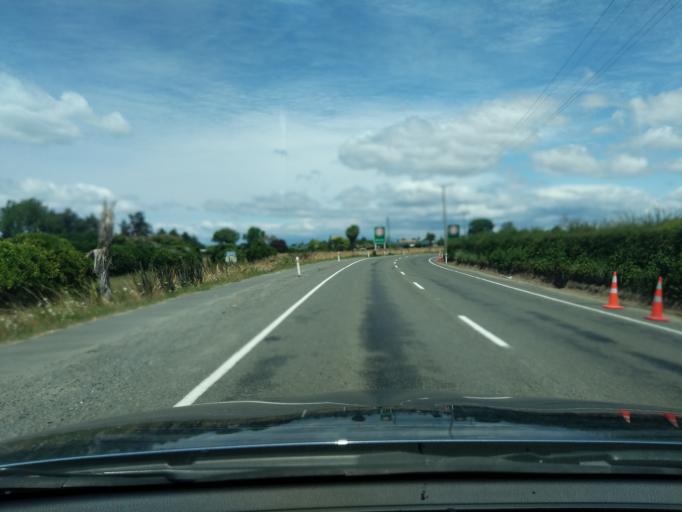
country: NZ
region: Tasman
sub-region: Tasman District
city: Motueka
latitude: -41.1009
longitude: 173.0124
